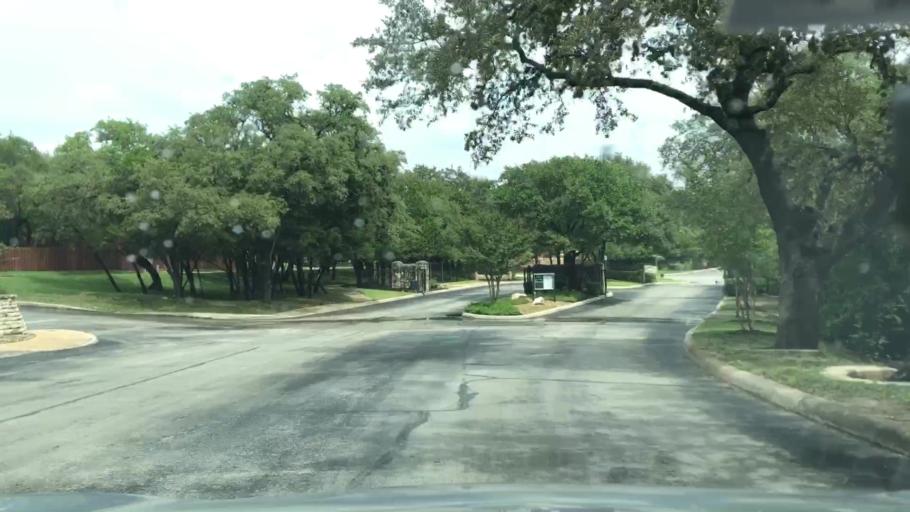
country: US
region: Texas
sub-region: Bexar County
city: Shavano Park
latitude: 29.5992
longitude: -98.5347
